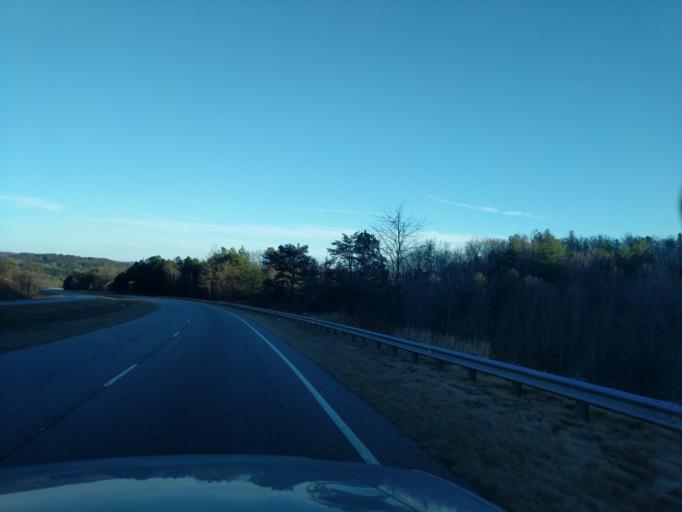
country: US
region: Georgia
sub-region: Stephens County
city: Toccoa
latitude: 34.5545
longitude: -83.3819
